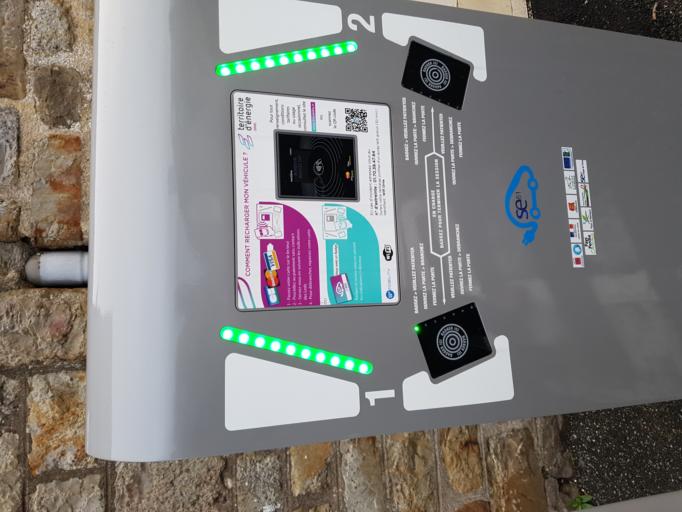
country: FR
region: Lower Normandy
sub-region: Departement de l'Orne
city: Domfront
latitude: 48.5943
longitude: -0.6508
